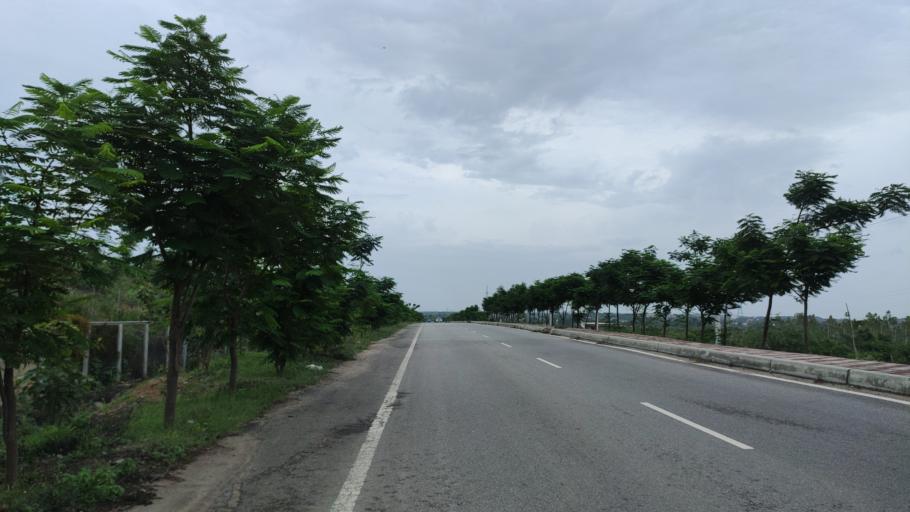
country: IN
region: Telangana
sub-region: Rangareddi
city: Secunderabad
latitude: 17.5794
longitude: 78.5877
